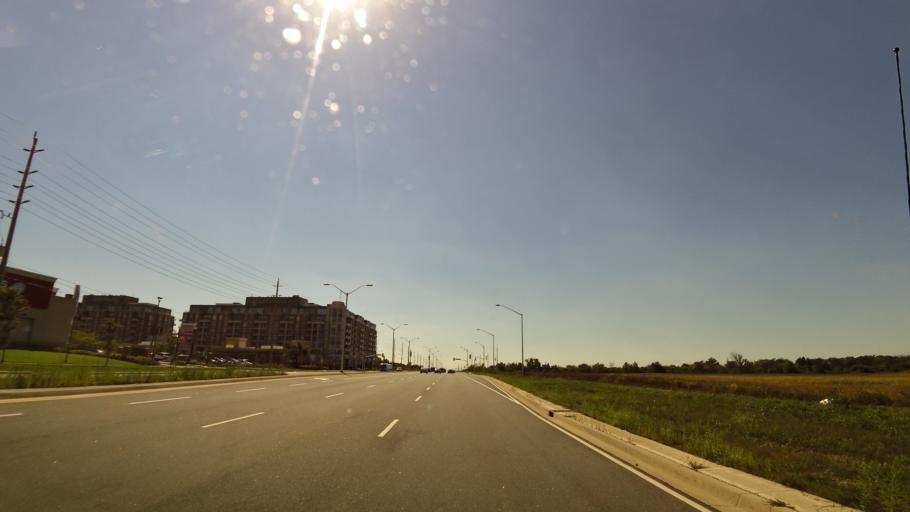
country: CA
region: Ontario
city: Oakville
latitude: 43.4994
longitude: -79.7072
